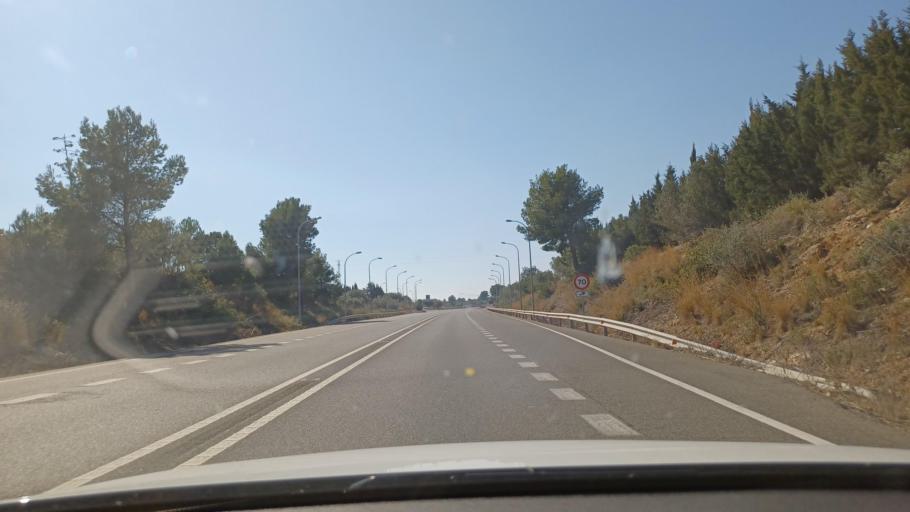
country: ES
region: Catalonia
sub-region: Provincia de Tarragona
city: l'Ametlla de Mar
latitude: 40.9042
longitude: 0.8061
